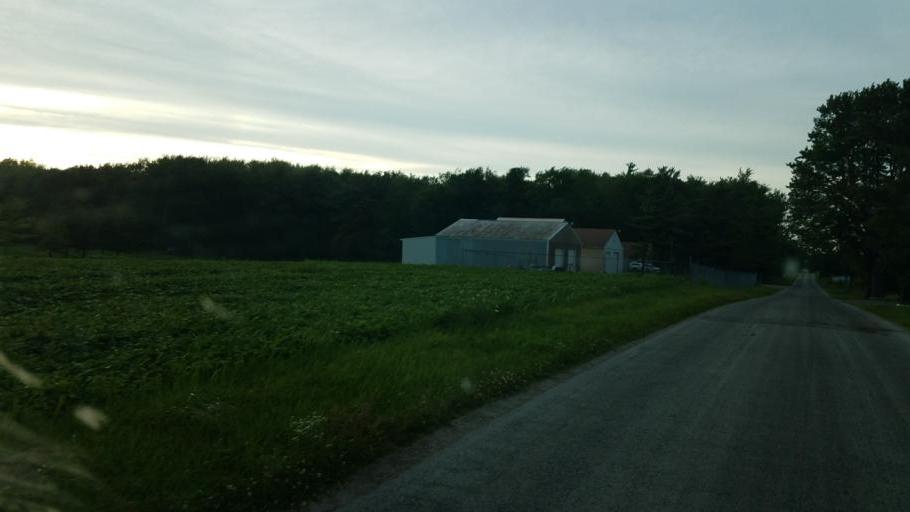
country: US
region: Ohio
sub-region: Huron County
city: Greenwich
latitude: 40.9199
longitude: -82.4746
